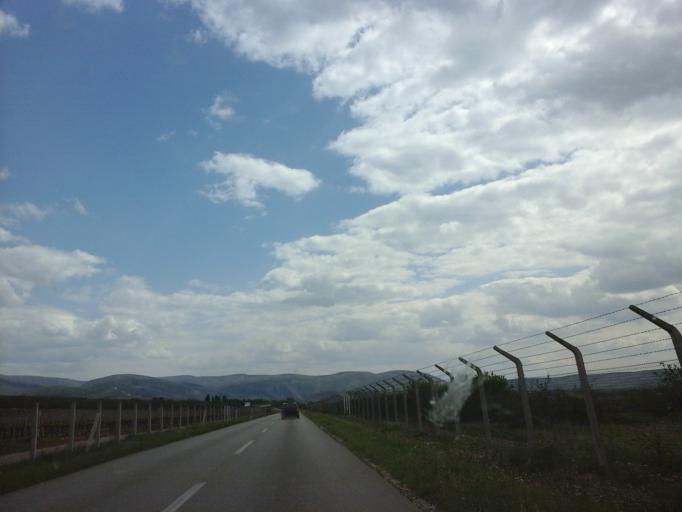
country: BA
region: Federation of Bosnia and Herzegovina
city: Blagaj
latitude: 43.2863
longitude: 17.8495
